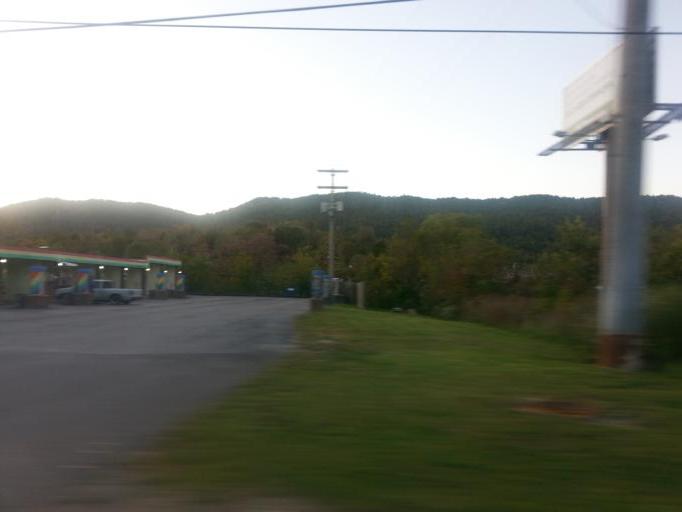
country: US
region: Tennessee
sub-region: Campbell County
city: Hunter
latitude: 36.3543
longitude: -84.1484
